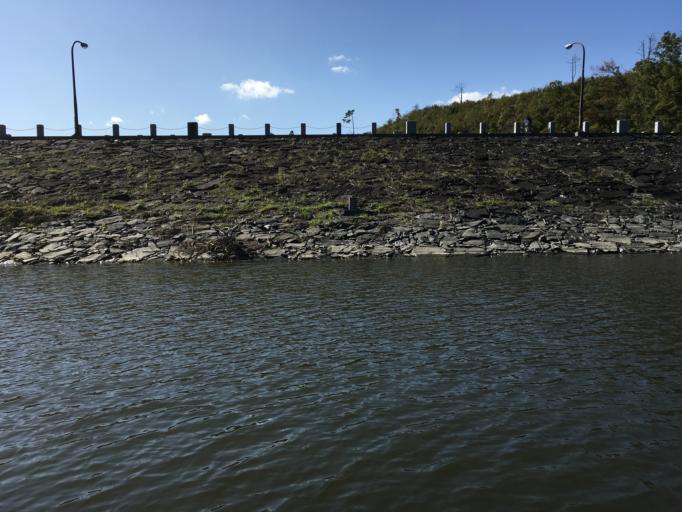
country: JP
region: Iwate
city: Ichinoseki
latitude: 38.7959
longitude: 141.2834
